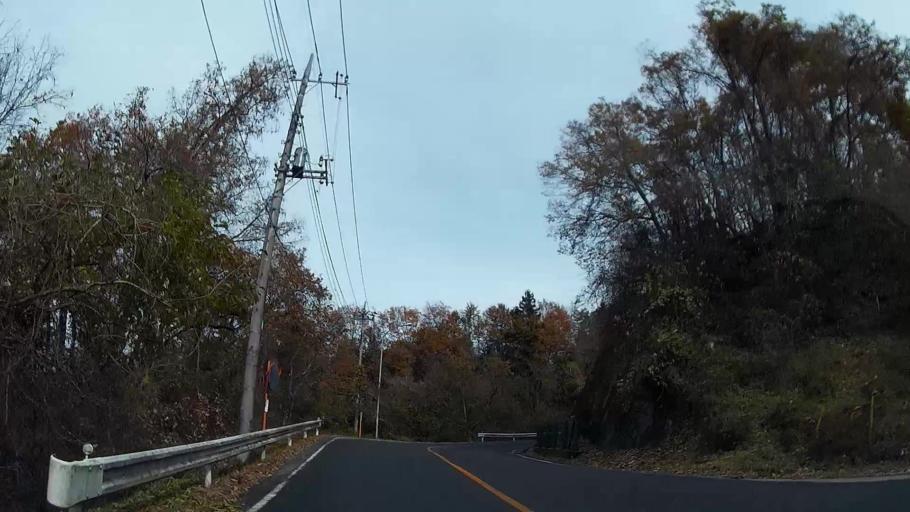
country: JP
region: Saitama
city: Chichibu
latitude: 35.9793
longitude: 139.0397
